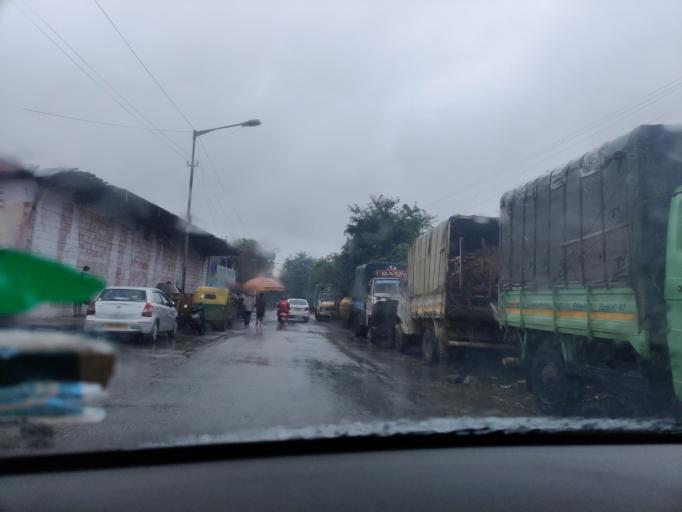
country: IN
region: Karnataka
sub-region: Bangalore Urban
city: Bangalore
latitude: 12.9964
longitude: 77.6632
